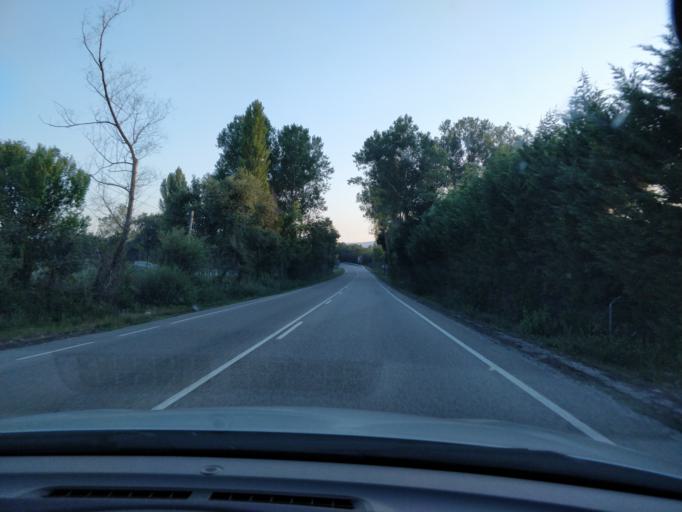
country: ES
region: Castille and Leon
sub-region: Provincia de Burgos
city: Medina de Pomar
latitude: 42.9616
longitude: -3.5515
